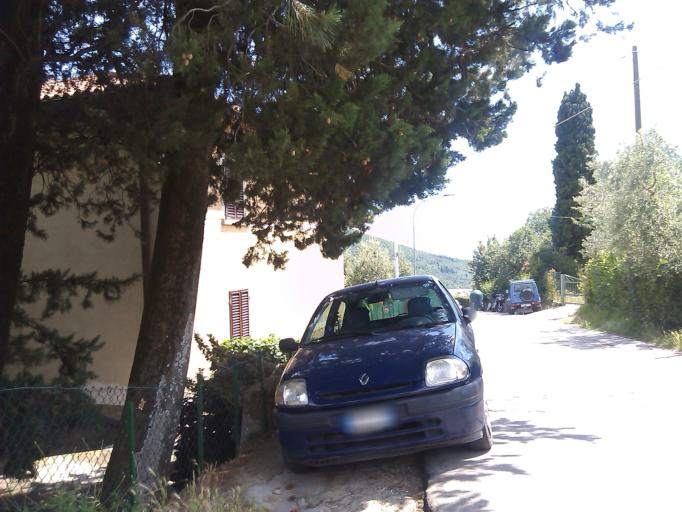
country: IT
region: Tuscany
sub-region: Provincia di Prato
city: Montemurlo
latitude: 43.9643
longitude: 11.0424
